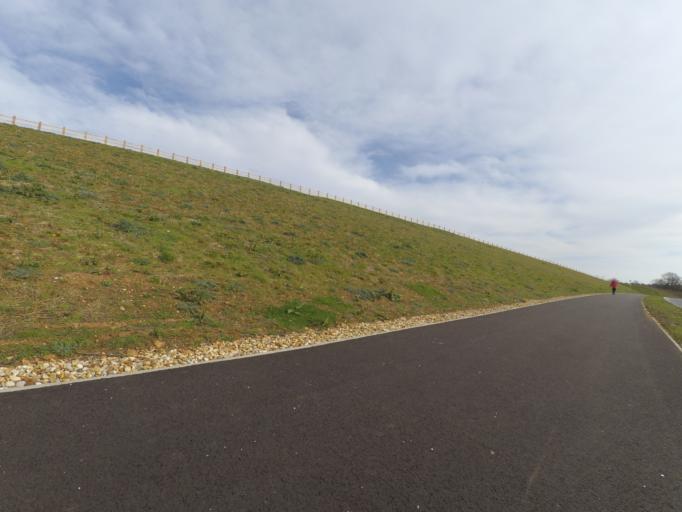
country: GB
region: England
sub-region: Warwickshire
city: Rugby
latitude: 52.3739
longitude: -1.2250
